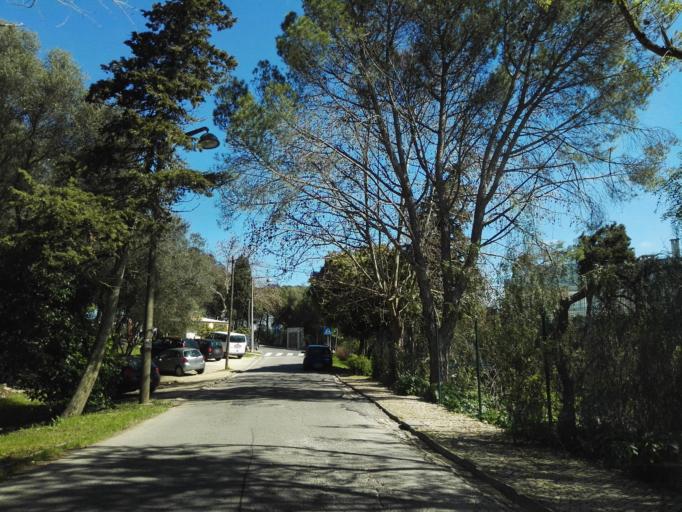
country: PT
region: Lisbon
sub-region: Sintra
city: Rio de Mouro
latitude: 38.7513
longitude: -9.3488
